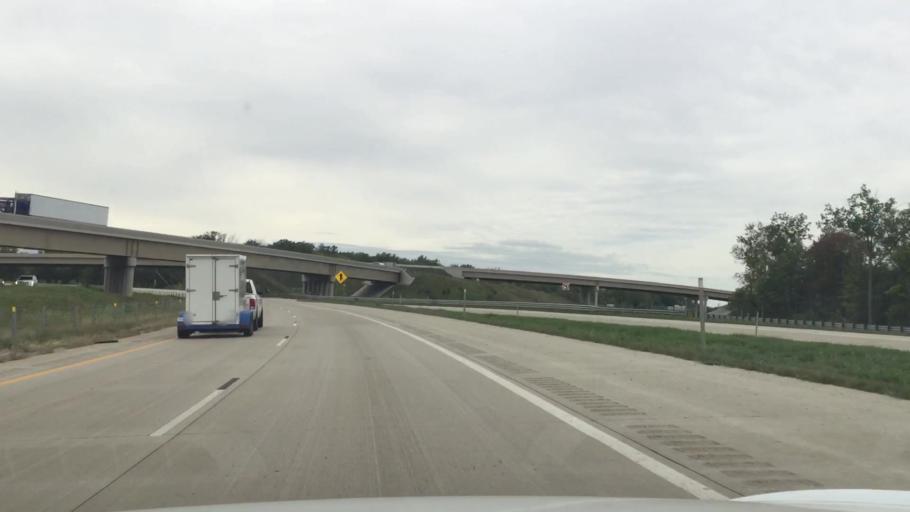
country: US
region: Michigan
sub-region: Saint Clair County
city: Marysville
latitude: 42.9737
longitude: -82.4866
